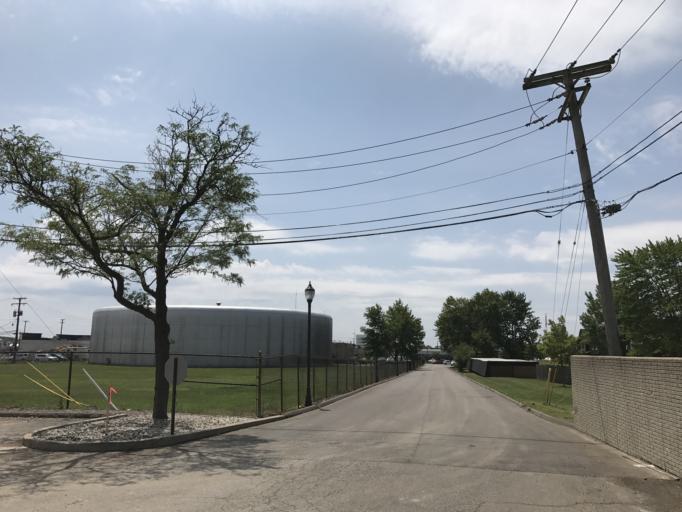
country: US
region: Michigan
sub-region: Oakland County
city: Bingham Farms
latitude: 42.5031
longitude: -83.2875
